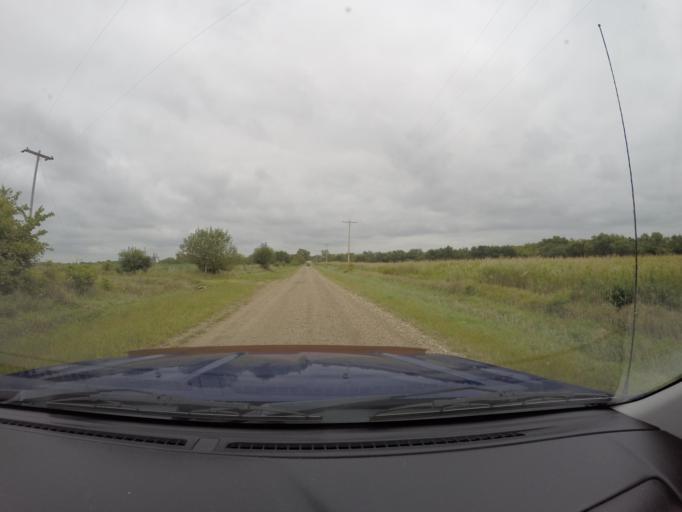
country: US
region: Kansas
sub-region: Morris County
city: Council Grove
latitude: 38.8624
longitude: -96.4978
